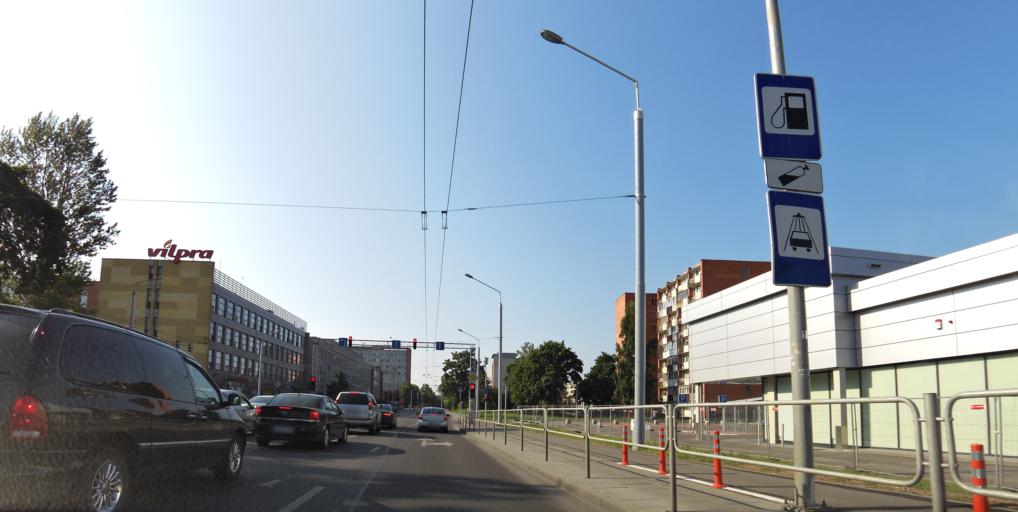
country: LT
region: Vilnius County
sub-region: Vilnius
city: Vilnius
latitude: 54.7140
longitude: 25.2867
